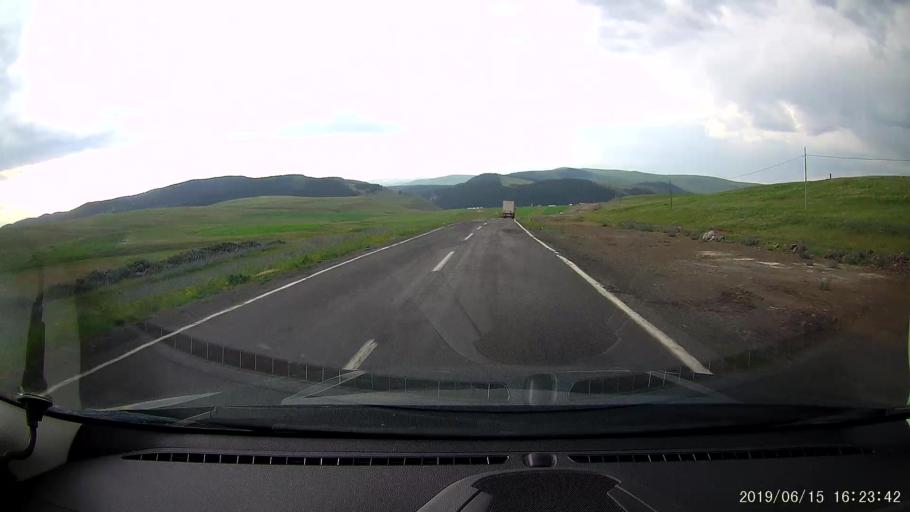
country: TR
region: Ardahan
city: Hanak
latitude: 41.1748
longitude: 42.8645
